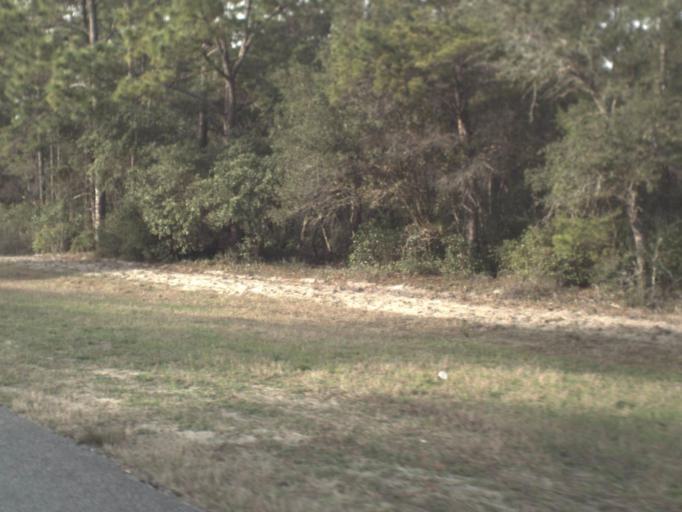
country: US
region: Florida
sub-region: Bay County
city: Mexico Beach
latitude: 29.9661
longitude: -85.4490
